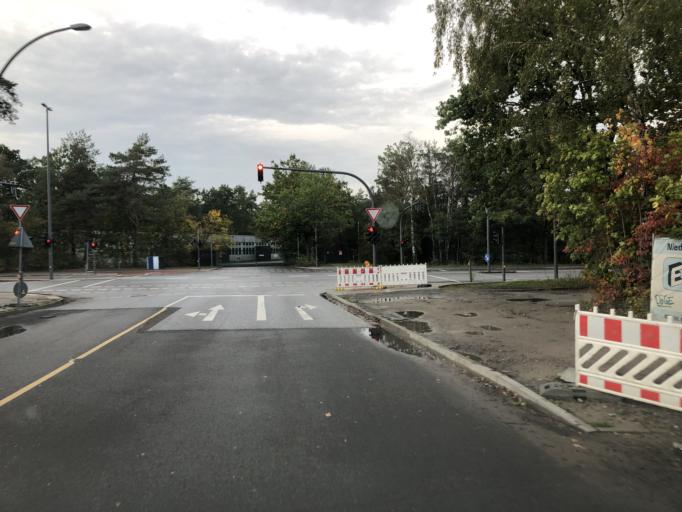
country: DE
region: Lower Saxony
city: Neu Wulmstorf
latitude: 53.4670
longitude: 9.8101
